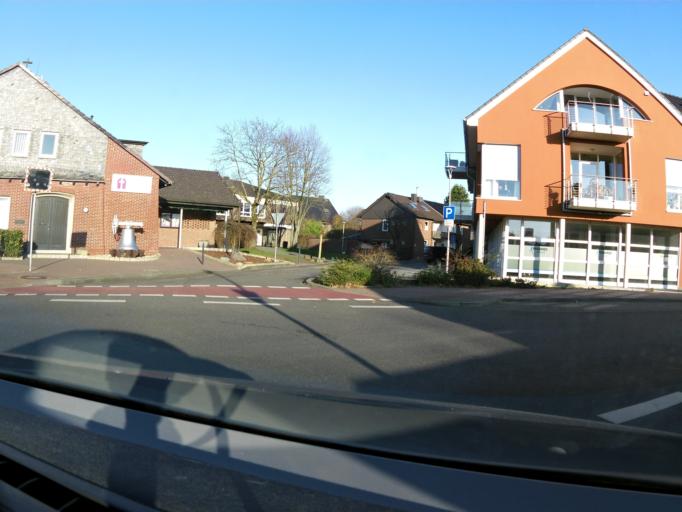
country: DE
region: North Rhine-Westphalia
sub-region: Regierungsbezirk Dusseldorf
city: Bruggen
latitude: 51.2431
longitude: 6.1836
